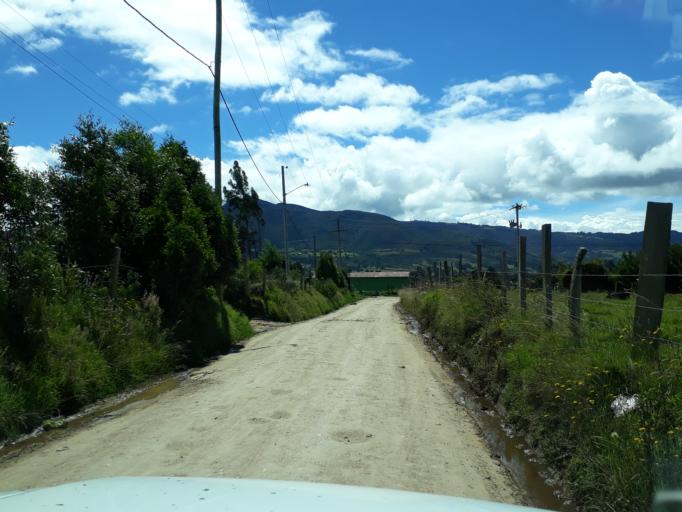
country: CO
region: Cundinamarca
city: Guasca
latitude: 4.8616
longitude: -73.8788
